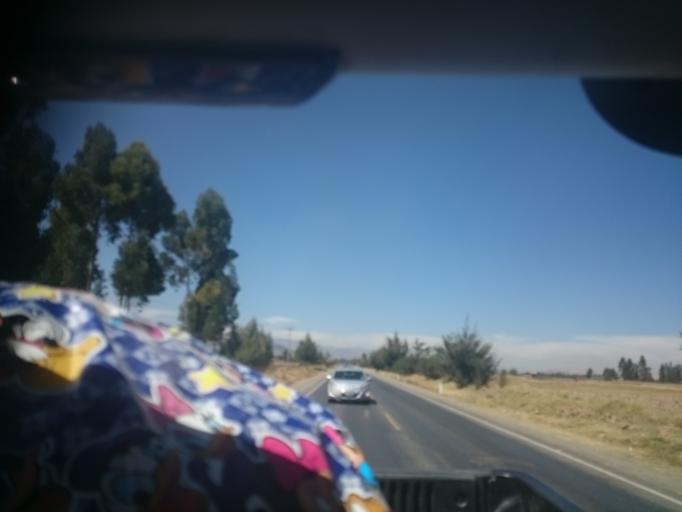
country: PE
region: Junin
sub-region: Provincia de Jauja
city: Huamali
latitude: -11.8242
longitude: -75.4100
